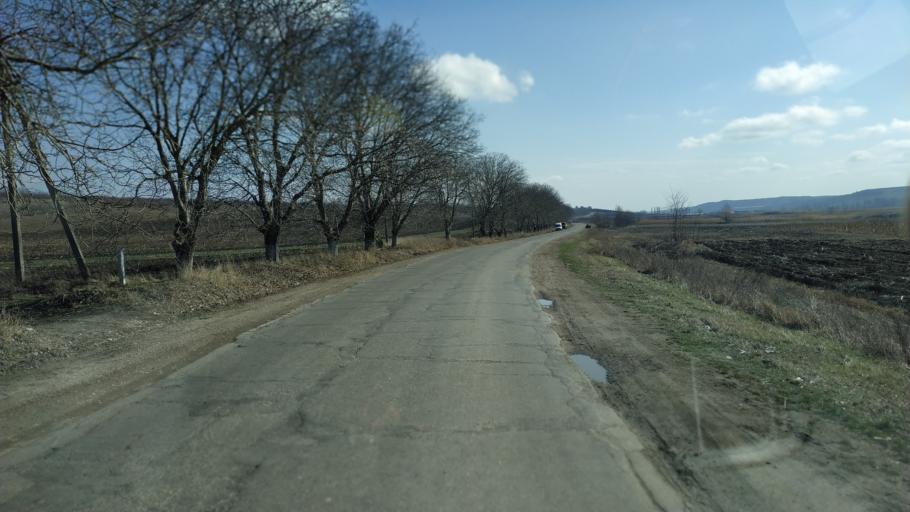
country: MD
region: Laloveni
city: Ialoveni
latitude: 46.9278
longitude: 28.6750
